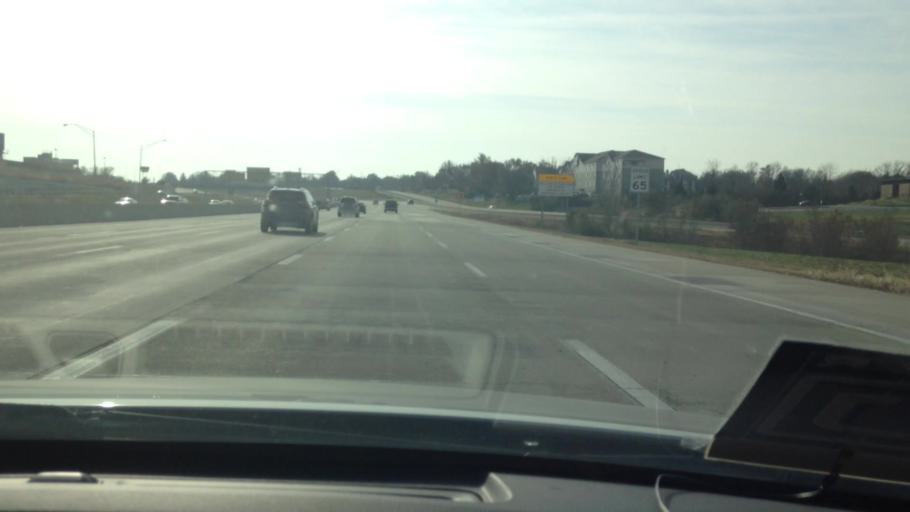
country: US
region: Missouri
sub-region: Jackson County
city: Grandview
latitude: 38.9222
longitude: -94.5281
